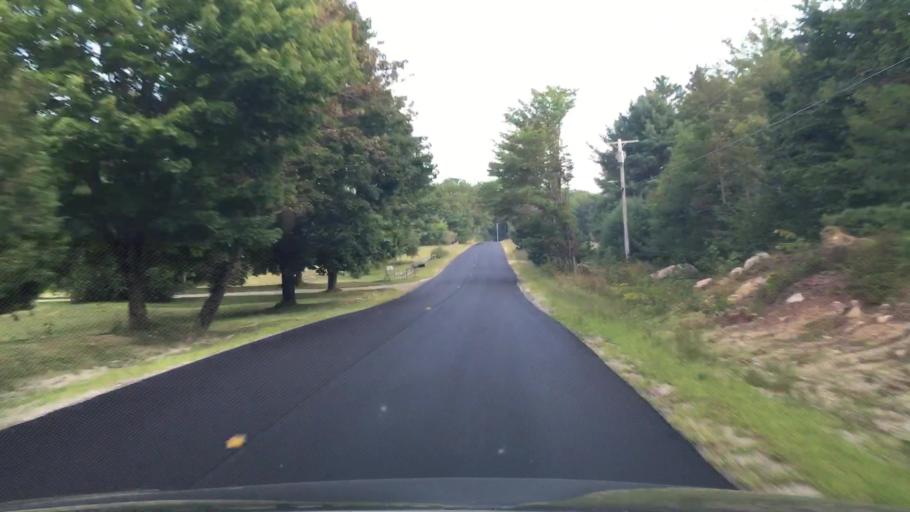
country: US
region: Maine
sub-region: Hancock County
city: Surry
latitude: 44.5284
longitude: -68.6114
